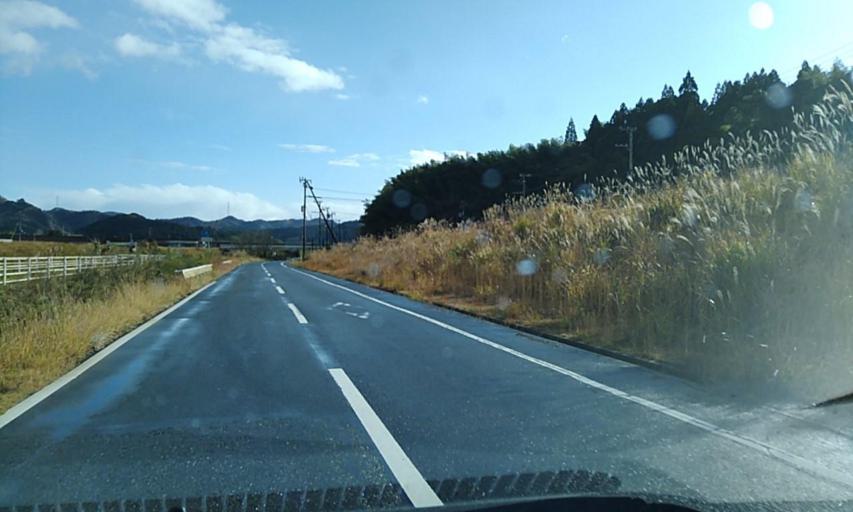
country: JP
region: Kyoto
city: Fukuchiyama
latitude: 35.3974
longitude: 135.1493
